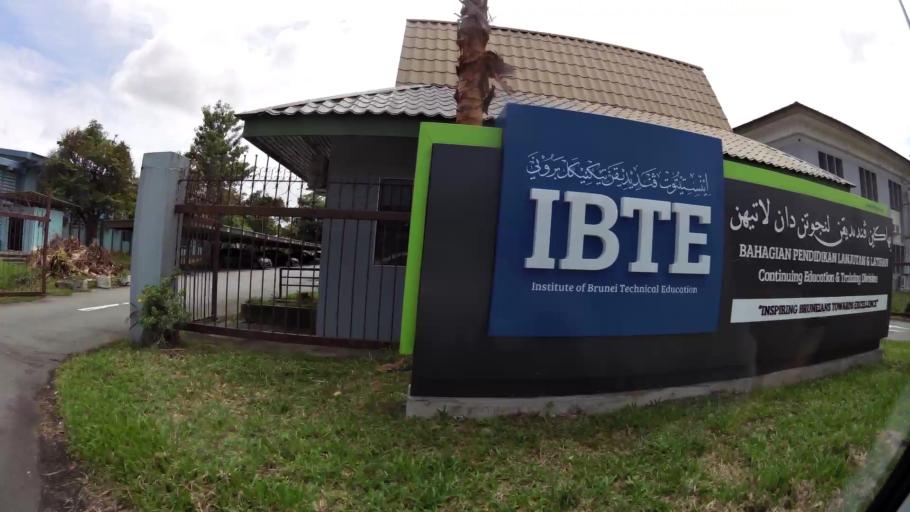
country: BN
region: Brunei and Muara
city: Bandar Seri Begawan
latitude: 4.9058
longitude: 114.9111
